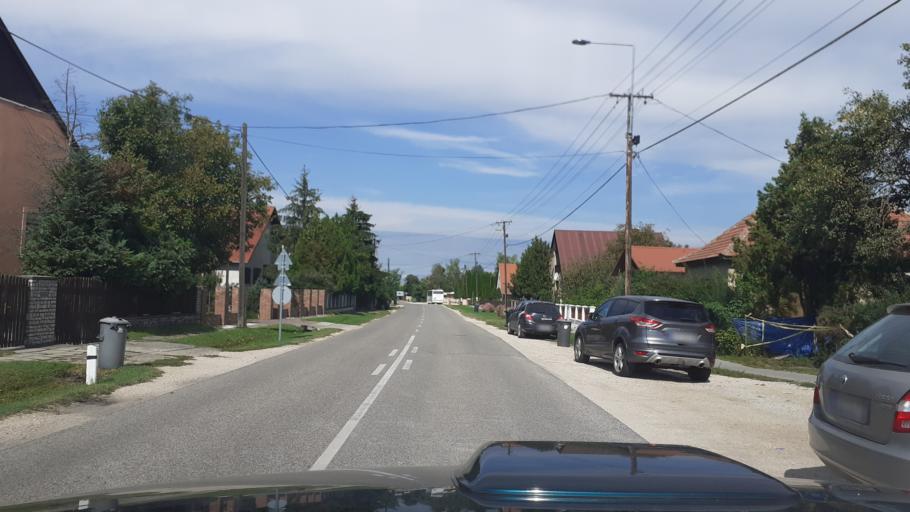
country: HU
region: Fejer
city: Pakozd
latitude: 47.1752
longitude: 18.5654
